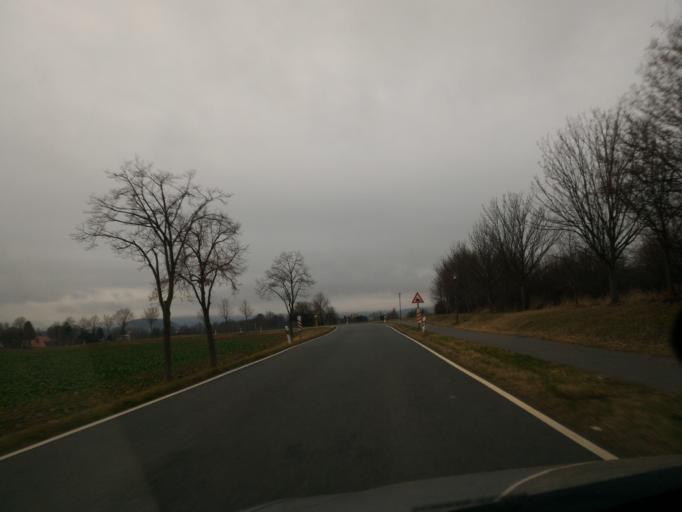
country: DE
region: Saxony
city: Leutersdorf
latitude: 50.9475
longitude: 14.6300
